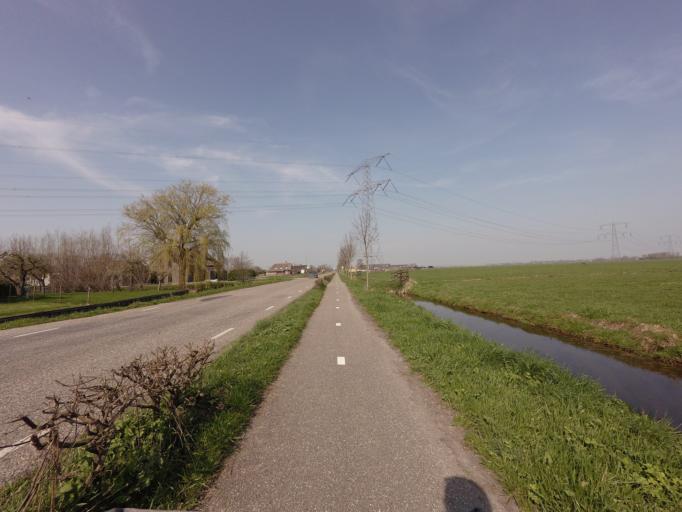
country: NL
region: Utrecht
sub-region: Stichtse Vecht
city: Breukelen
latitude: 52.1445
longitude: 4.9760
